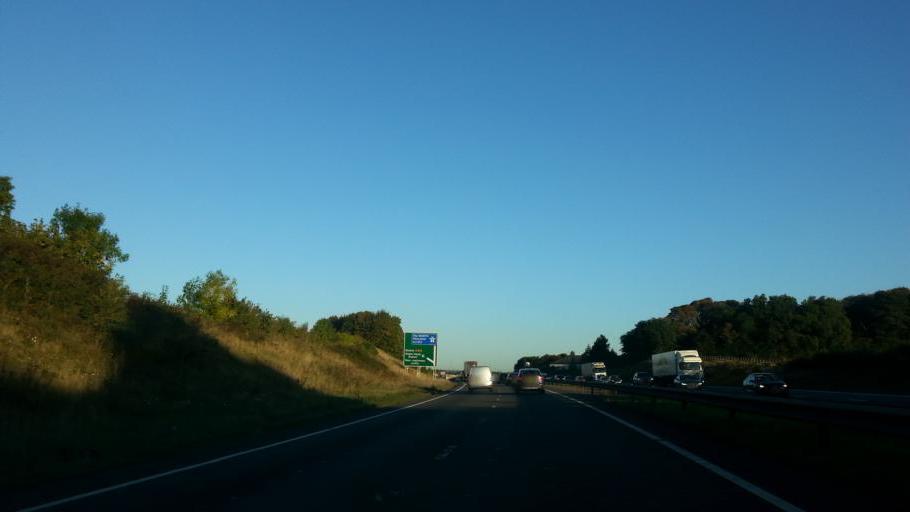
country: GB
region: England
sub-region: Nottinghamshire
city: Bircotes
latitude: 53.3843
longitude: -1.0576
